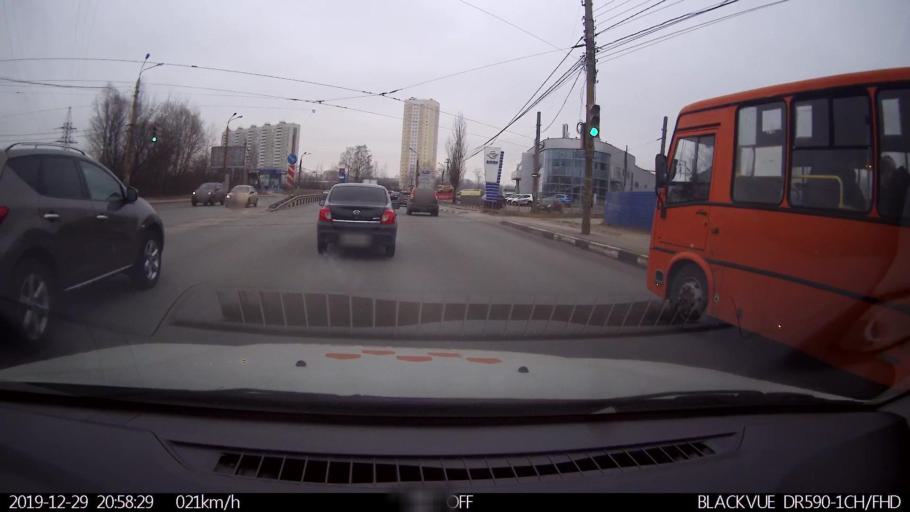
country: RU
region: Nizjnij Novgorod
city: Nizhniy Novgorod
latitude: 56.3038
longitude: 43.9162
